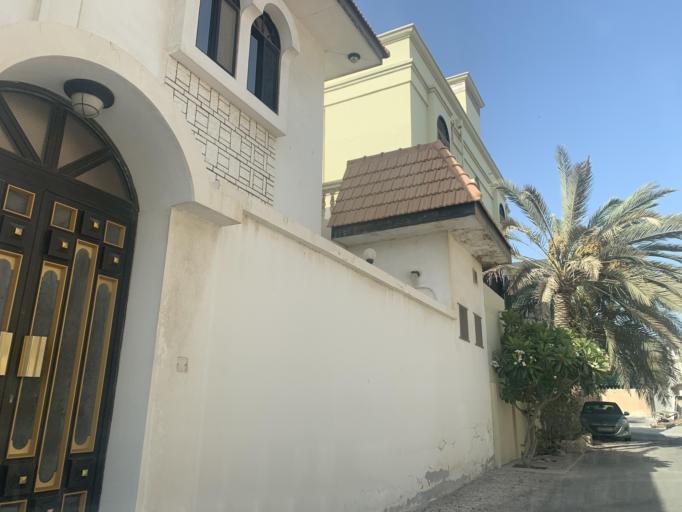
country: BH
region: Manama
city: Jidd Hafs
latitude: 26.2108
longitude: 50.4518
